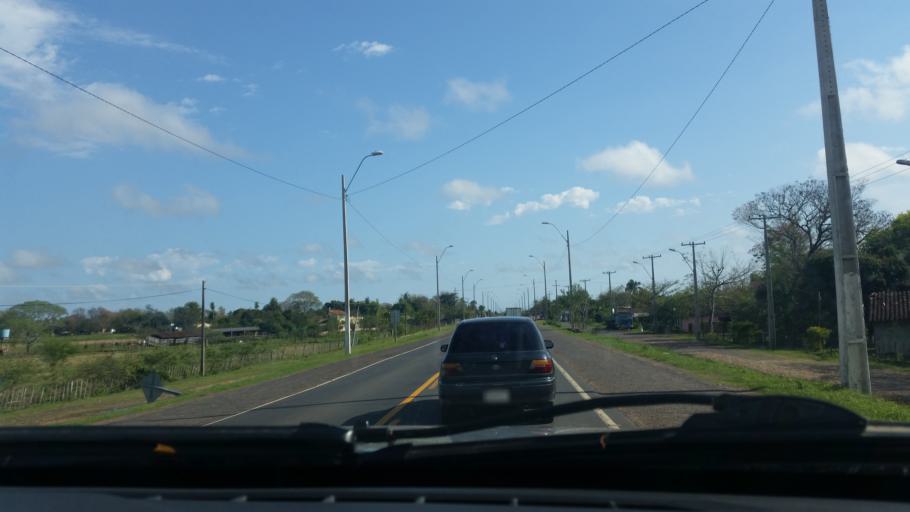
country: PY
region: Presidente Hayes
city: Benjamin Aceval
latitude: -24.9571
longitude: -57.5489
